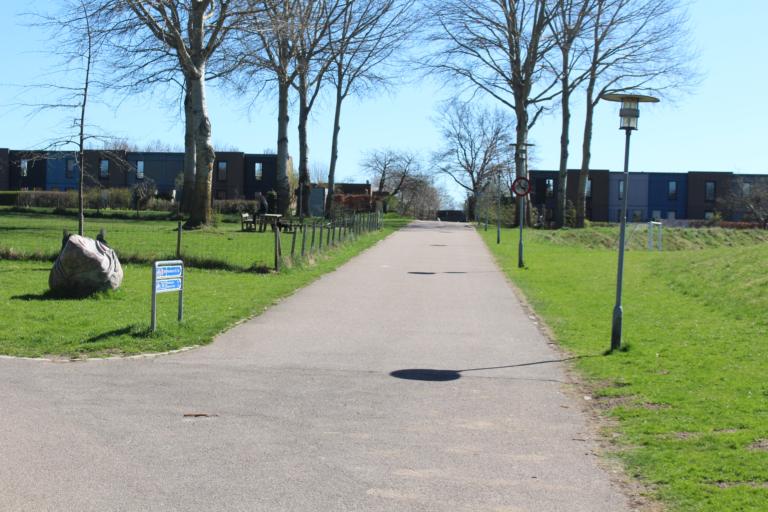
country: DK
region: Capital Region
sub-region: Albertslund Kommune
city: Albertslund
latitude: 55.6782
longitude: 12.3442
